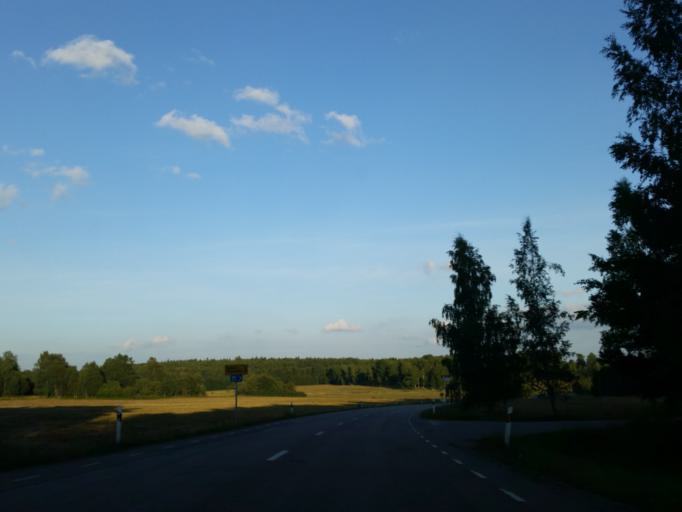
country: SE
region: Stockholm
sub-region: Sodertalje Kommun
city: Soedertaelje
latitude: 59.2288
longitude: 17.5568
